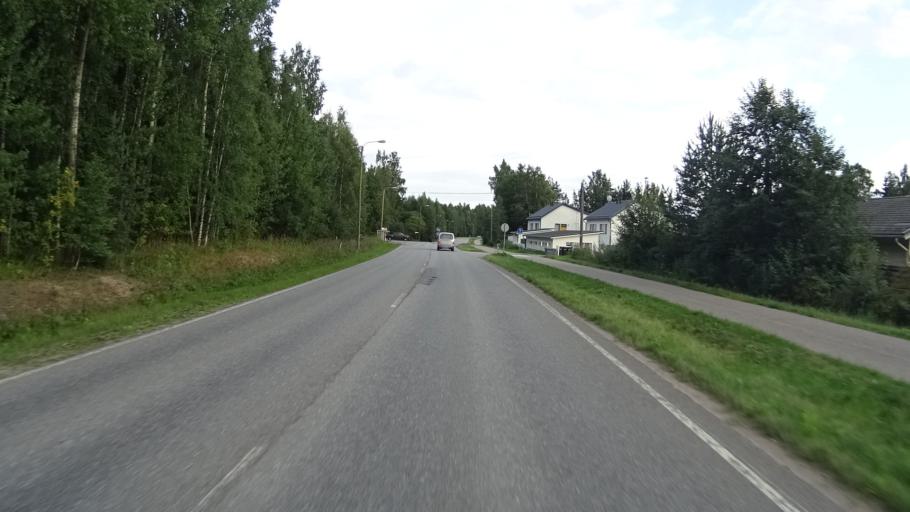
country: FI
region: Uusimaa
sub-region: Helsinki
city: Kilo
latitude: 60.3268
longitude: 24.8661
